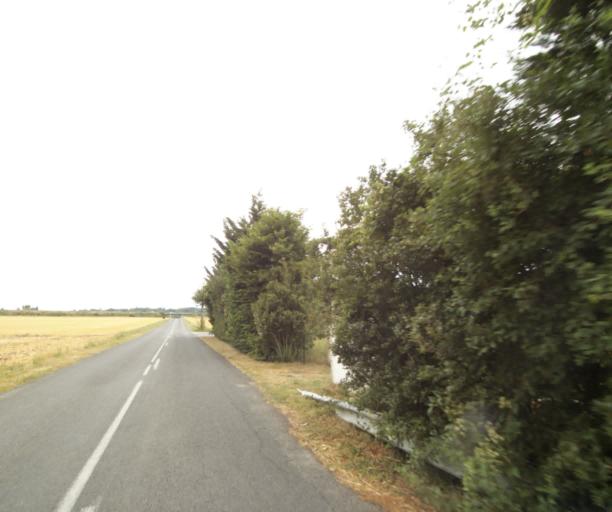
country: FR
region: Ile-de-France
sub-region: Departement de Seine-et-Marne
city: Cely
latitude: 48.4712
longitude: 2.5216
